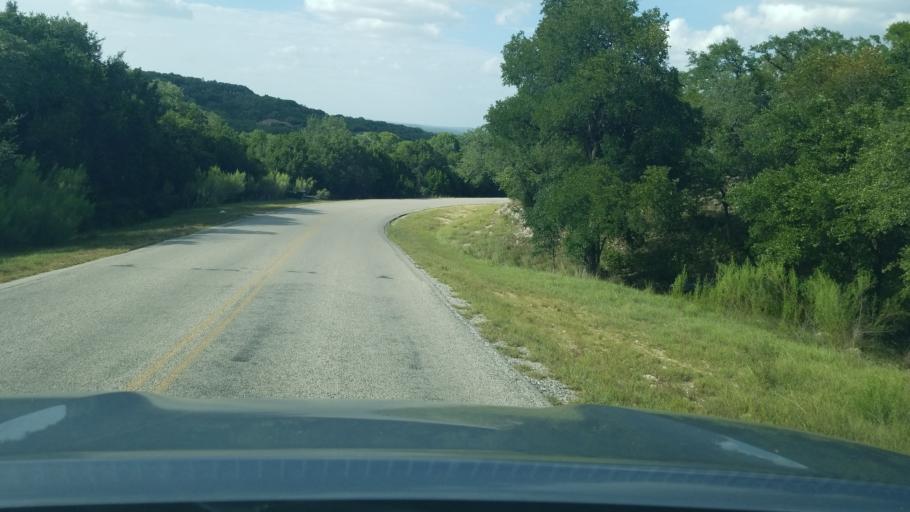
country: US
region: Texas
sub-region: Comal County
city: Bulverde
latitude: 29.8082
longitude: -98.4081
